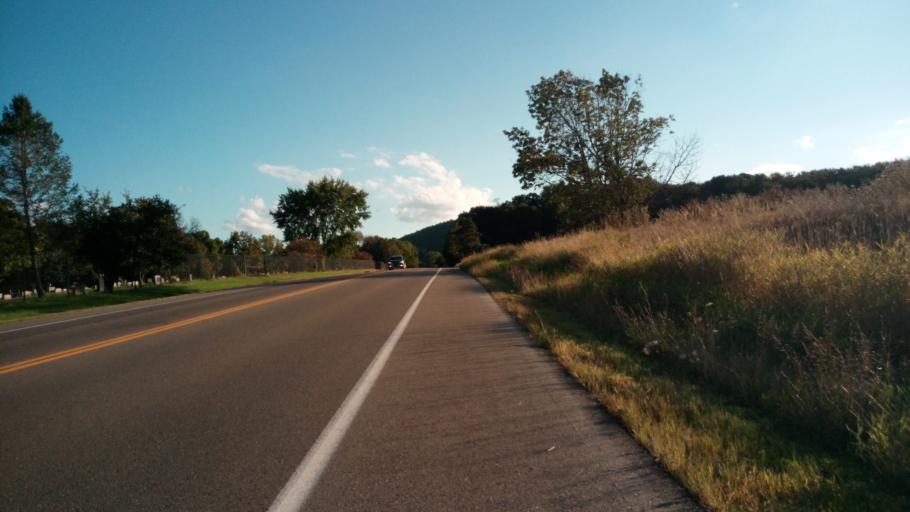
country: US
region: New York
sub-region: Chemung County
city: Elmira Heights
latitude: 42.1110
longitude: -76.8301
